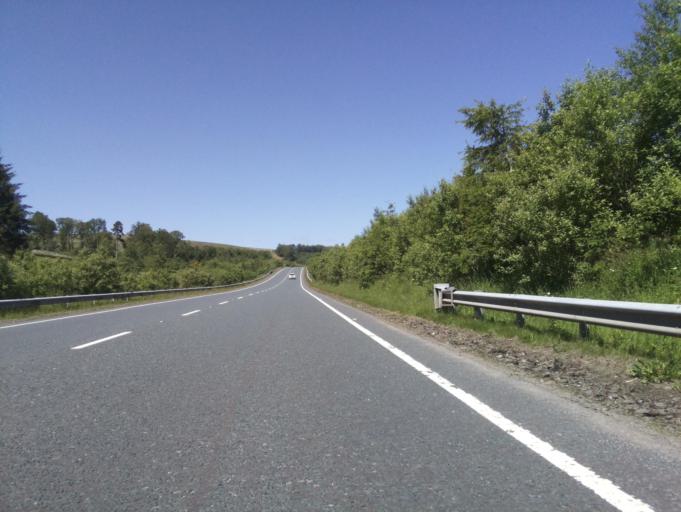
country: GB
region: Scotland
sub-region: Dumfries and Galloway
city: Langholm
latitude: 55.1178
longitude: -2.9883
